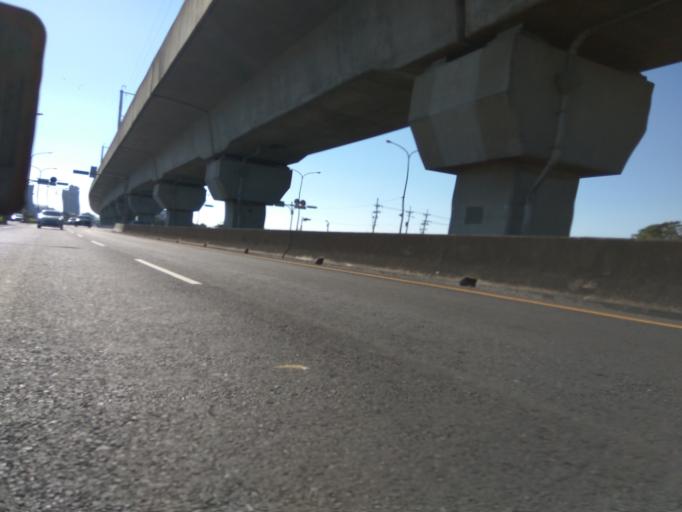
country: TW
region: Taiwan
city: Taoyuan City
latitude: 24.9677
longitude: 121.1701
